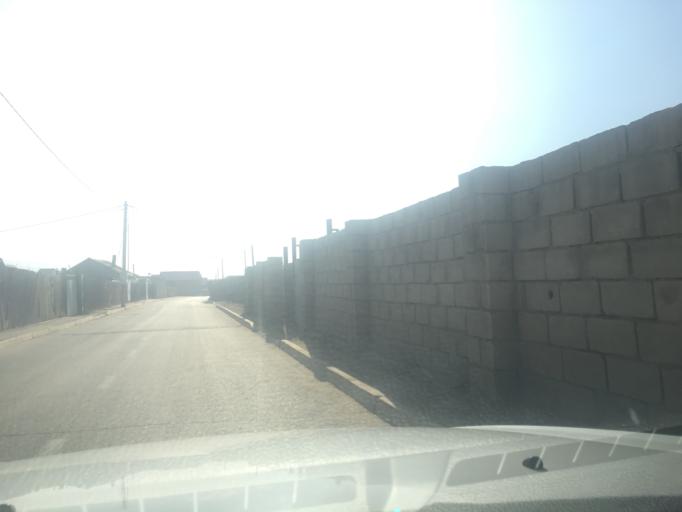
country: MN
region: Ulaanbaatar
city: Ulaanbaatar
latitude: 47.9666
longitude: 106.8270
